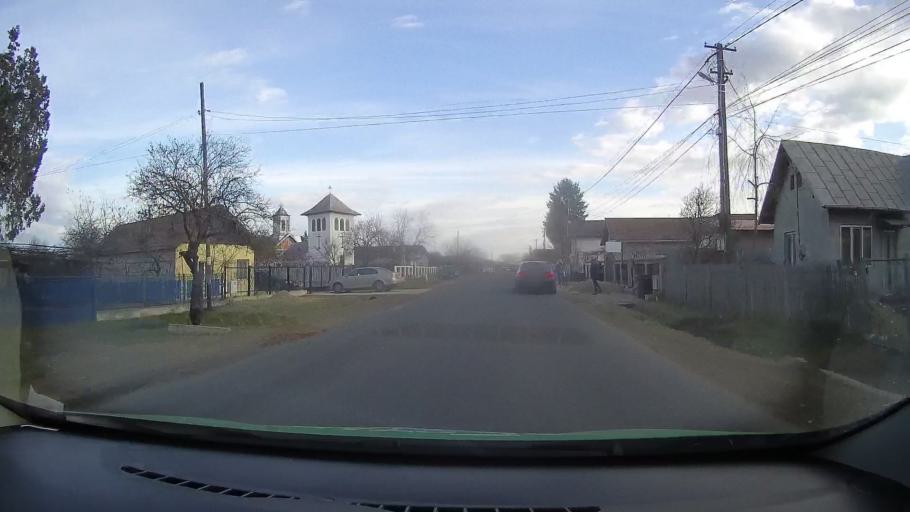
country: RO
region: Dambovita
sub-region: Municipiul Targoviste
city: Targoviste
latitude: 44.8930
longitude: 25.4596
